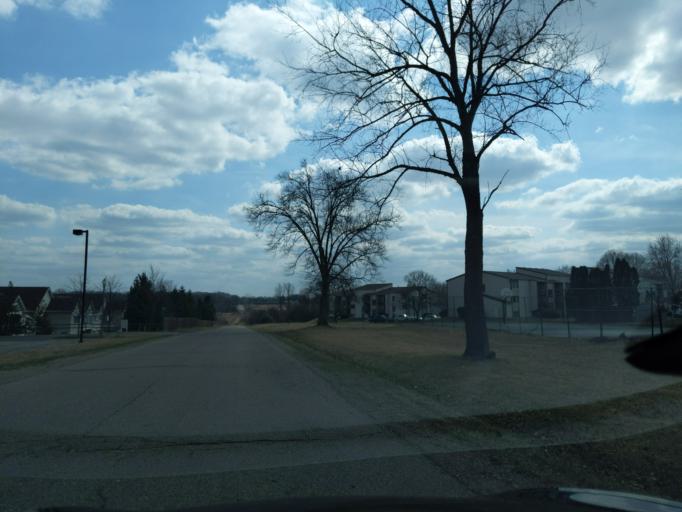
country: US
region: Michigan
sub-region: Jackson County
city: Jackson
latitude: 42.2748
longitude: -84.4429
